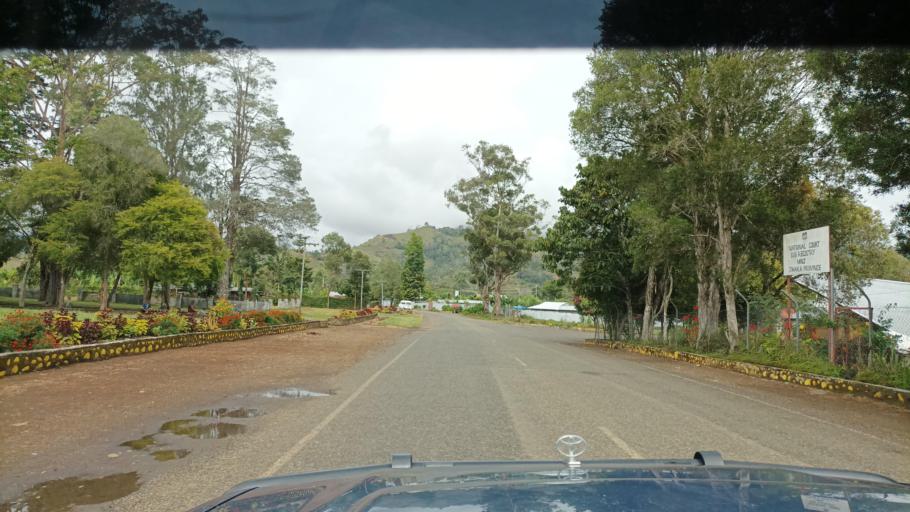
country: PG
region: Jiwaka
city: Minj
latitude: -5.9085
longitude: 144.6895
